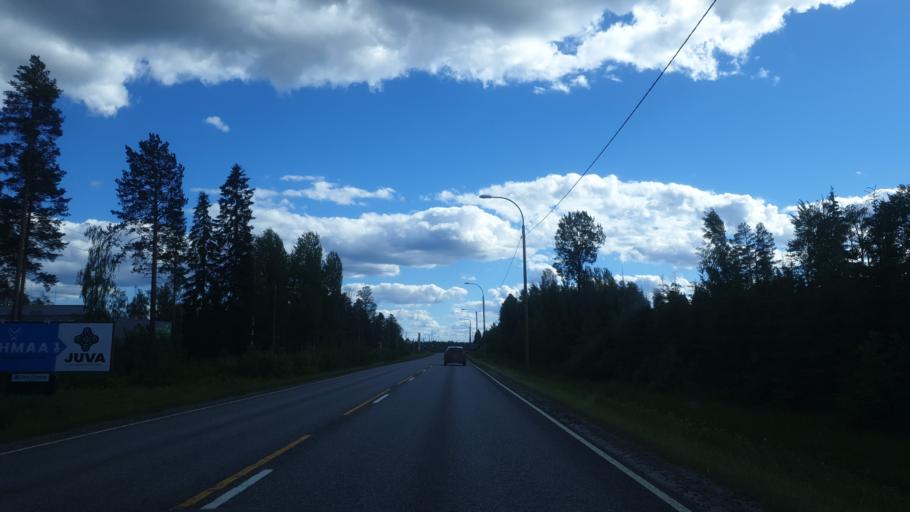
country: FI
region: Southern Savonia
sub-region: Pieksaemaeki
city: Juva
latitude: 61.9065
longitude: 27.8048
